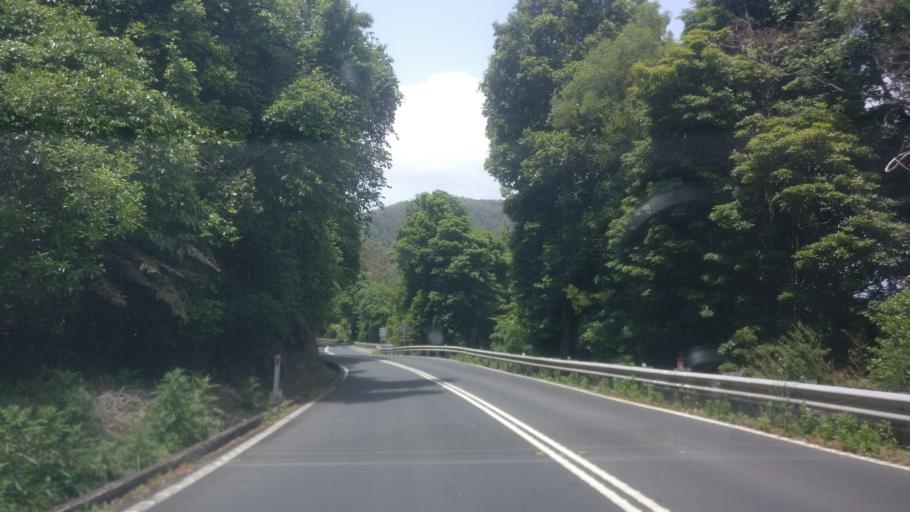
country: AU
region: New South Wales
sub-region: Shoalhaven Shire
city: Kangaroo Valley
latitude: -34.7909
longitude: 150.5586
